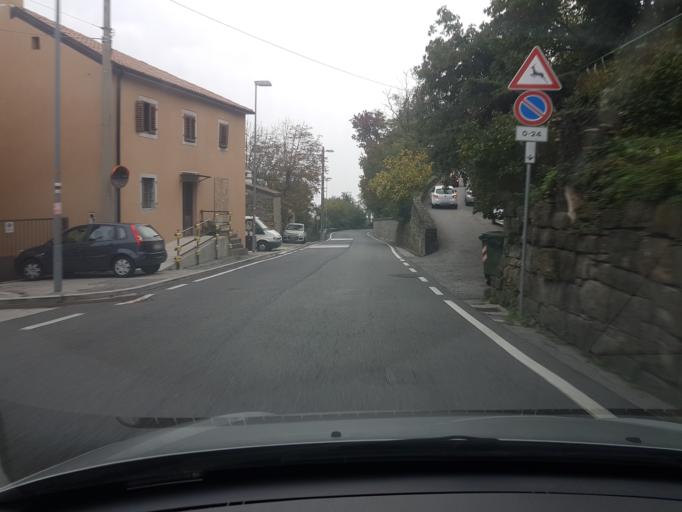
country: IT
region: Friuli Venezia Giulia
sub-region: Provincia di Trieste
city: Prosecco-Contovello
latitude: 45.7030
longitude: 13.7334
